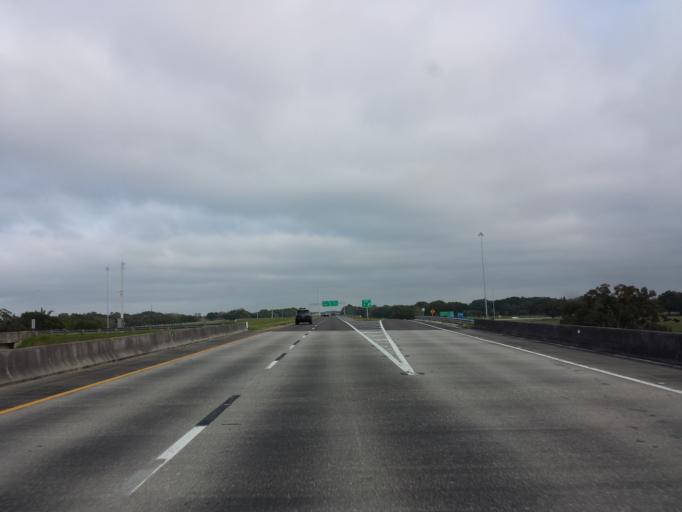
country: US
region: Florida
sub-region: Manatee County
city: Memphis
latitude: 27.5850
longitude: -82.5456
